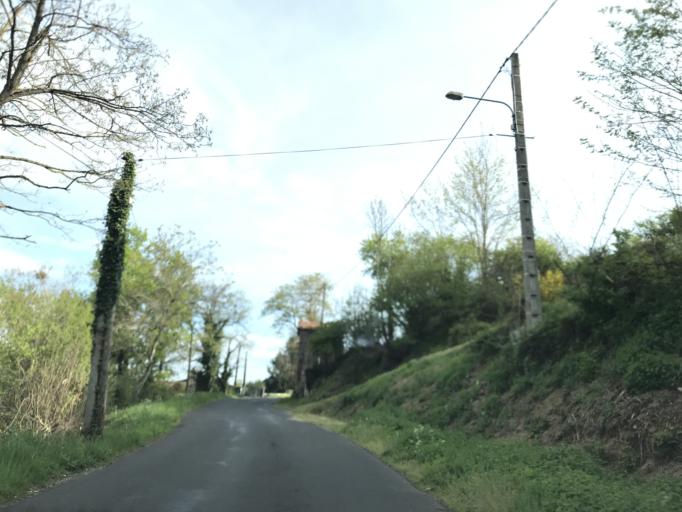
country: FR
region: Auvergne
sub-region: Departement du Puy-de-Dome
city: Courpiere
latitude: 45.7547
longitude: 3.5257
